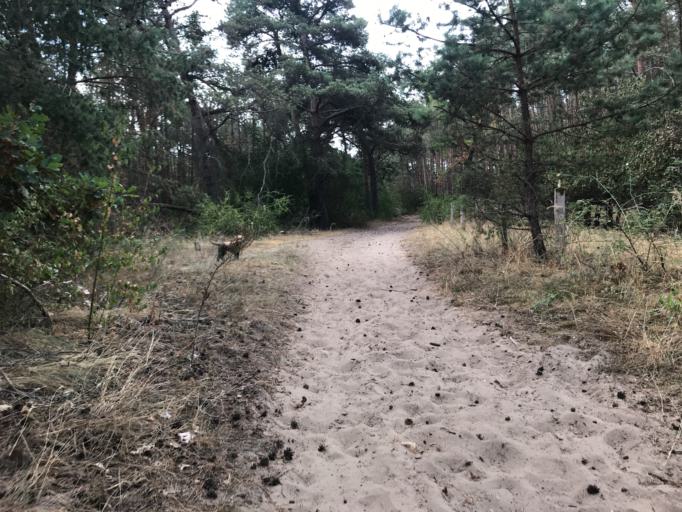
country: DE
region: Rheinland-Pfalz
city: Budenheim
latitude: 50.0051
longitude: 8.1430
